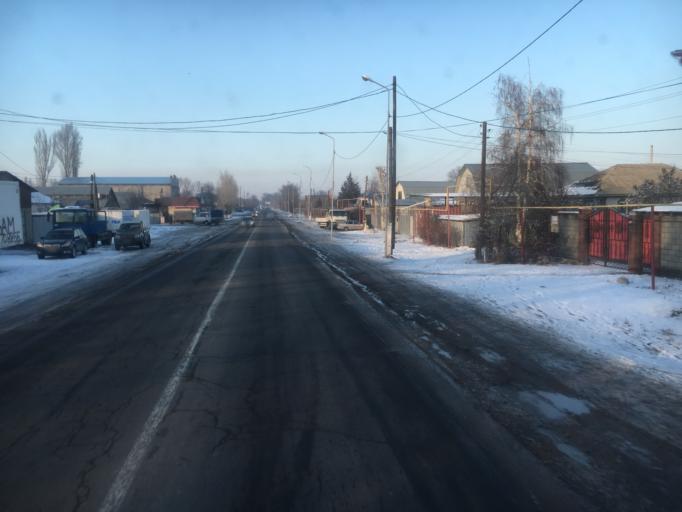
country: KZ
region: Almaty Oblysy
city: Burunday
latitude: 43.3687
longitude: 76.6414
